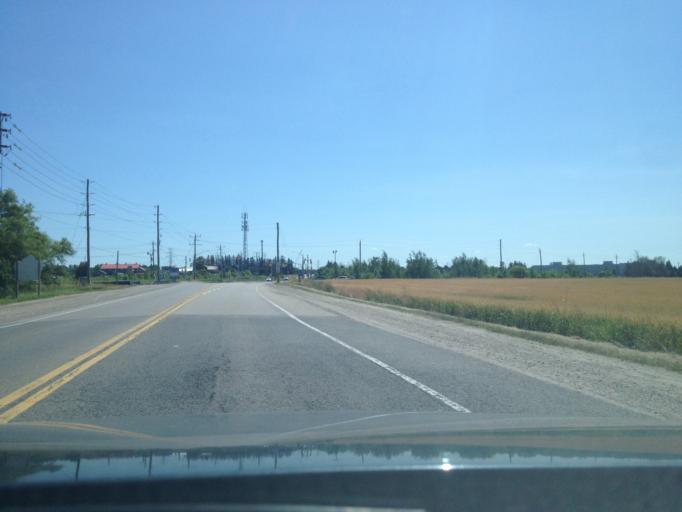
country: CA
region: Ontario
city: Waterloo
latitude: 43.5196
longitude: -80.5165
